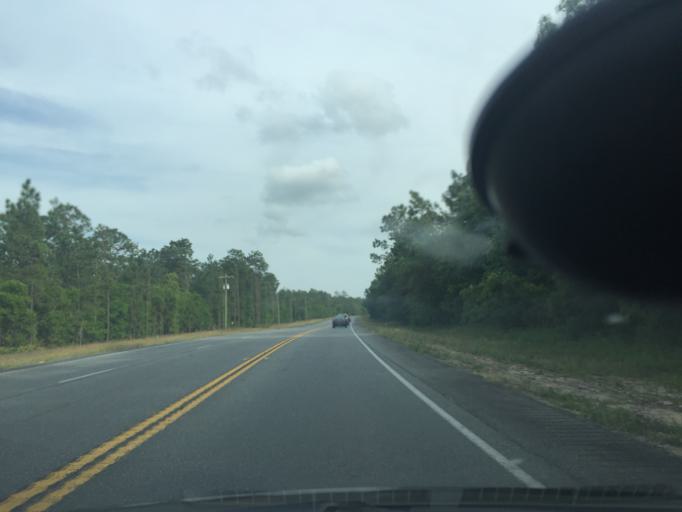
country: US
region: Georgia
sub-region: Chatham County
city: Bloomingdale
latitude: 32.0440
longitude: -81.3333
